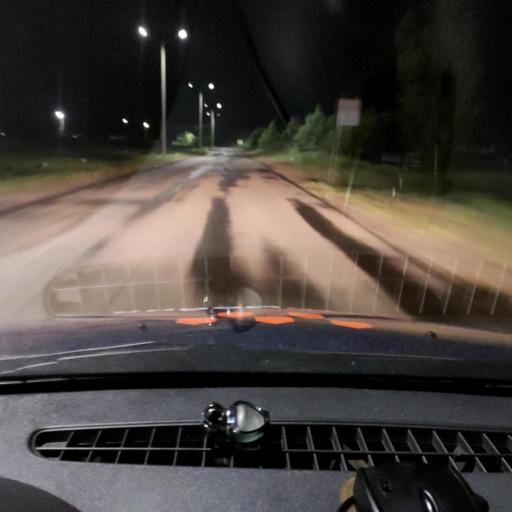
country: RU
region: Voronezj
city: Khrenovoye
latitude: 51.1194
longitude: 40.2654
